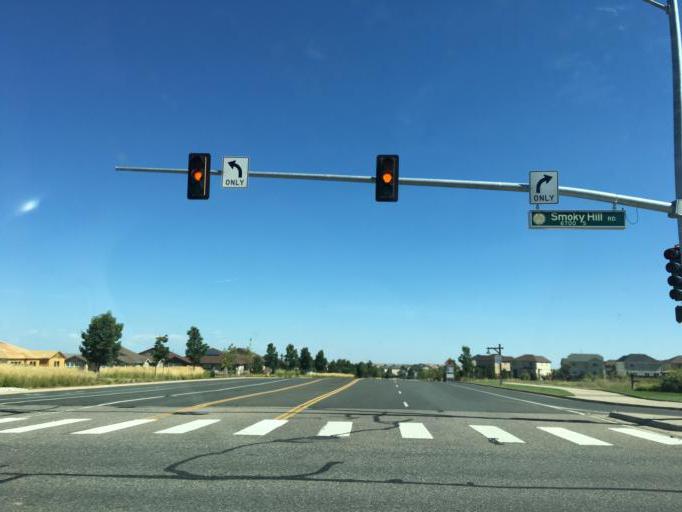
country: US
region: Colorado
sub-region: Douglas County
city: Parker
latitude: 39.5939
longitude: -104.6973
